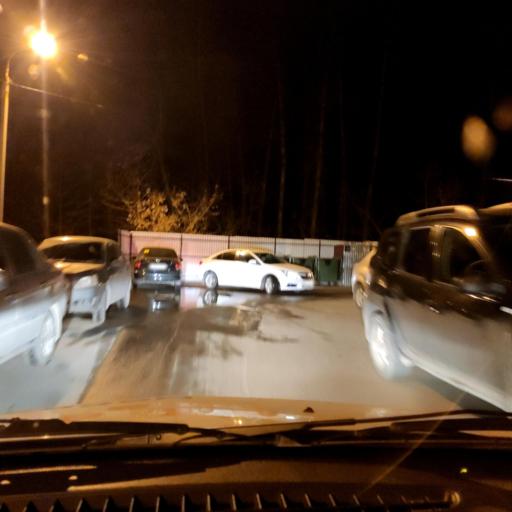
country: RU
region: Bashkortostan
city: Ufa
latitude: 54.7856
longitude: 56.1088
